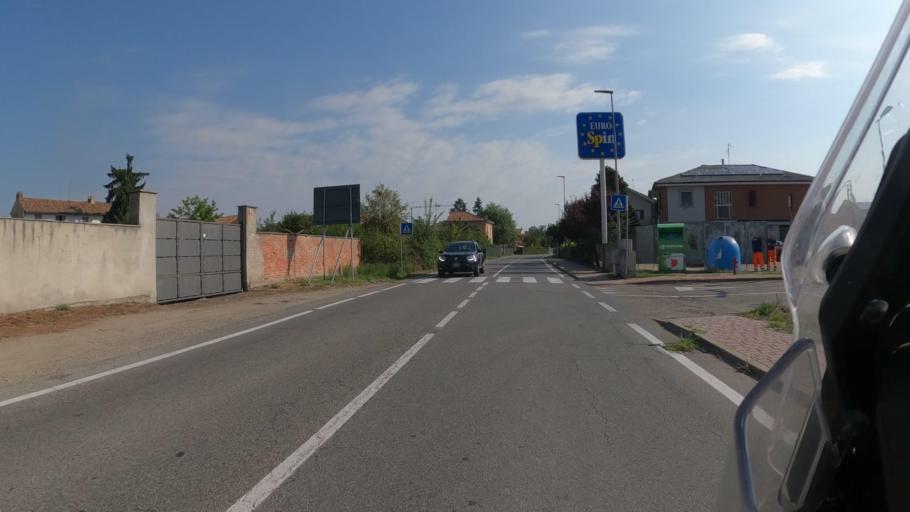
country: IT
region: Piedmont
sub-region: Provincia di Asti
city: Nizza Monferrato
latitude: 44.7765
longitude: 8.3631
